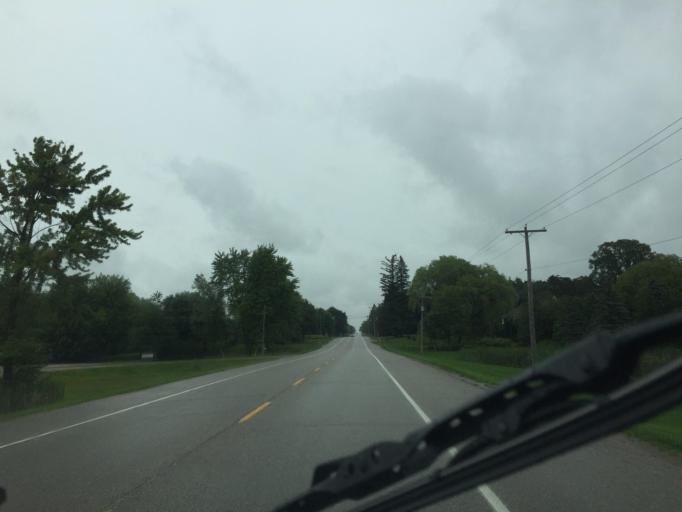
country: CA
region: Ontario
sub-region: Wellington County
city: Guelph
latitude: 43.4486
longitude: -80.2322
